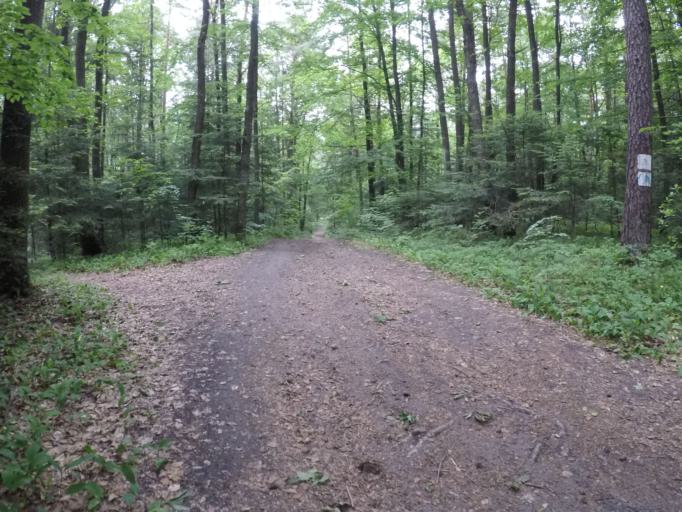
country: PL
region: Swietokrzyskie
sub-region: Powiat kielecki
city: Kielce
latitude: 50.8391
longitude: 20.6067
